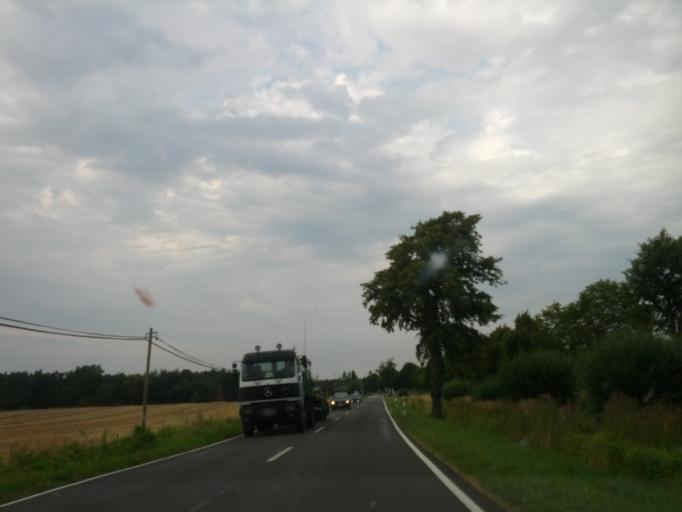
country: DE
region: Mecklenburg-Vorpommern
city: Kropelin
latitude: 54.0365
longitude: 11.7930
